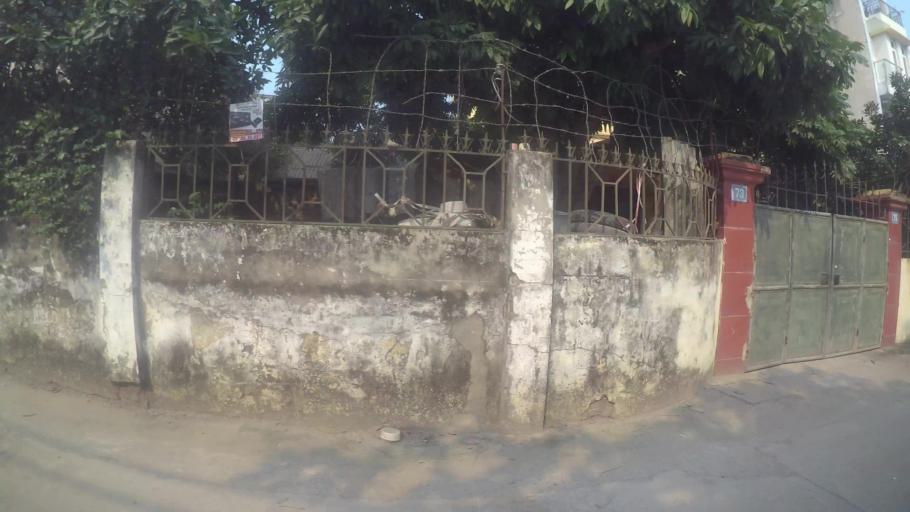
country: VN
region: Ha Noi
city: Ha Dong
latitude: 20.9934
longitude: 105.7538
